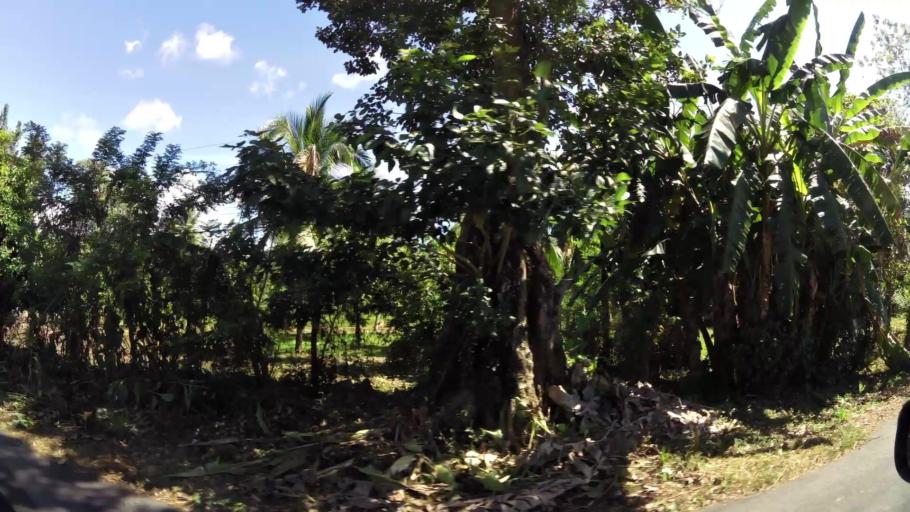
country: CR
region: Puntarenas
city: Quepos
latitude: 9.3257
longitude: -83.9582
